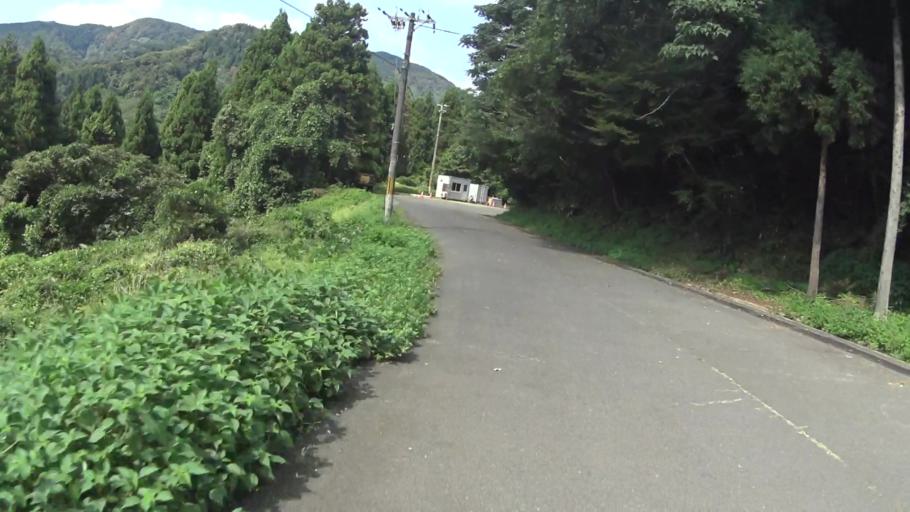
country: JP
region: Kyoto
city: Miyazu
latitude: 35.6783
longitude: 135.2372
